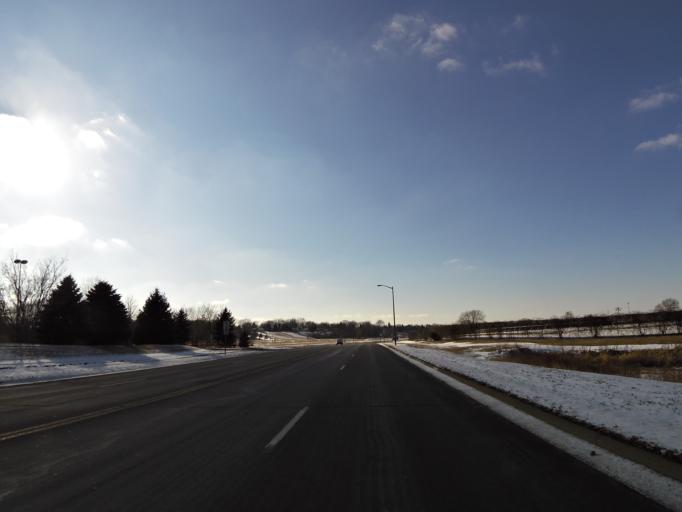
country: US
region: Minnesota
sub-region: Scott County
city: Shakopee
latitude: 44.7851
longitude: -93.4782
